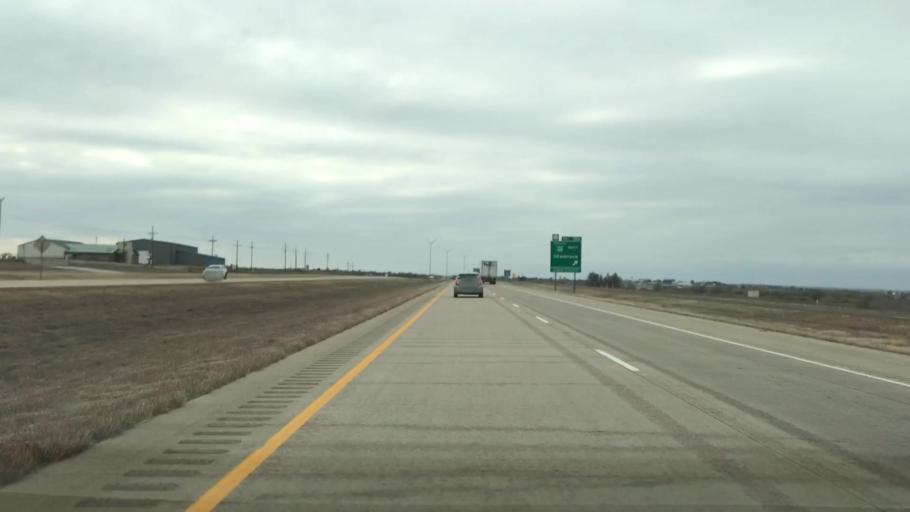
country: US
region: Texas
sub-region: Wheeler County
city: Shamrock
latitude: 35.2269
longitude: -100.2155
